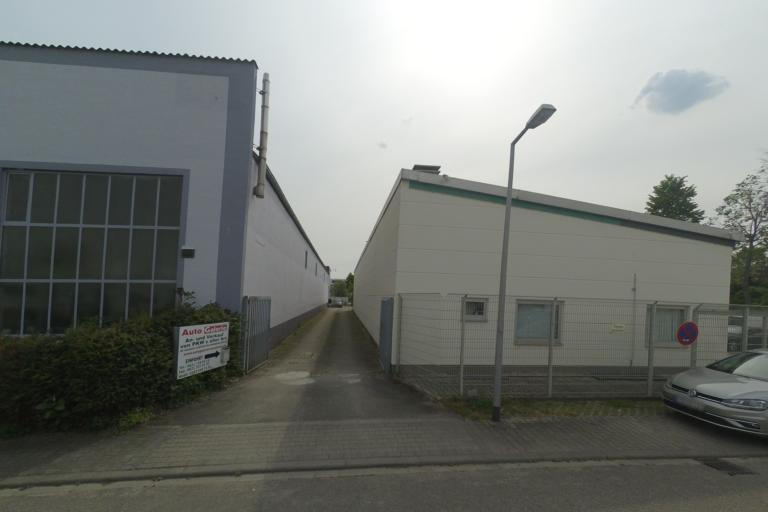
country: DE
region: Baden-Wuerttemberg
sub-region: Karlsruhe Region
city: Mannheim
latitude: 49.5117
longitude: 8.4953
